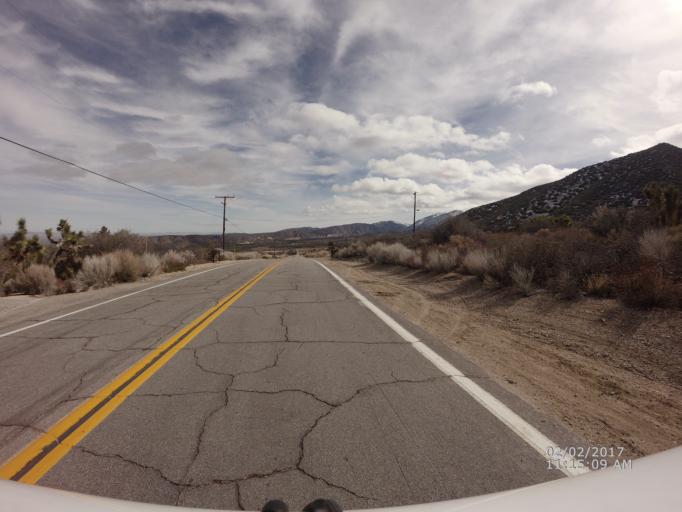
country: US
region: California
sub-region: Los Angeles County
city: Littlerock
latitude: 34.4263
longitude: -117.9144
